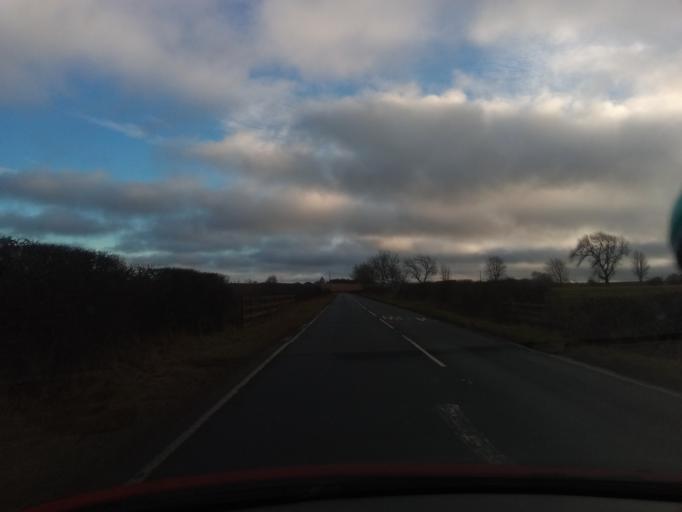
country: GB
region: England
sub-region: Northumberland
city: Rothley
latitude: 55.1205
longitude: -1.9116
